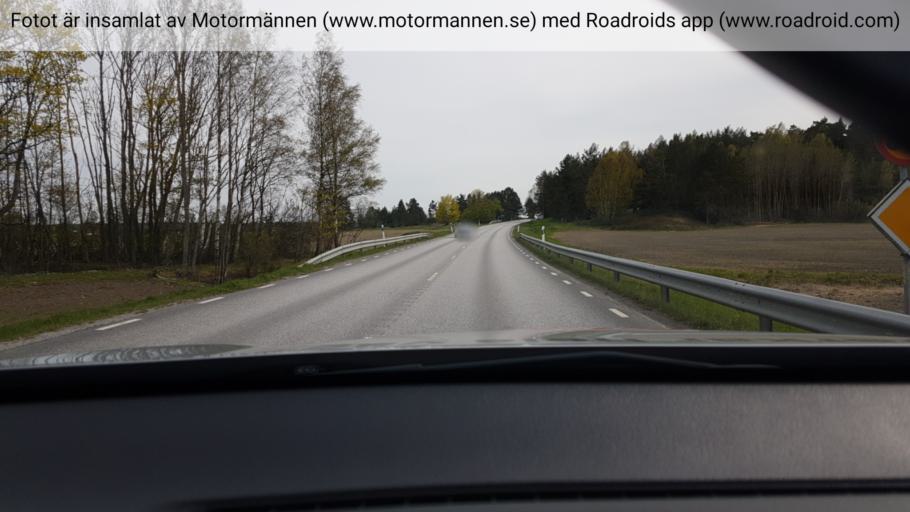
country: SE
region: Stockholm
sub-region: Vallentuna Kommun
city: Vallentuna
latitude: 59.6928
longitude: 18.0448
